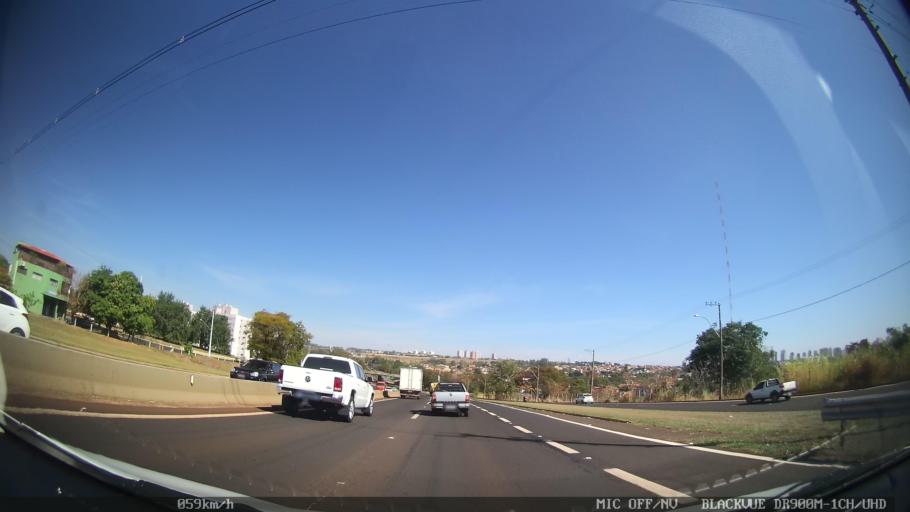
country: BR
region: Sao Paulo
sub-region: Ribeirao Preto
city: Ribeirao Preto
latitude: -21.2123
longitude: -47.7715
